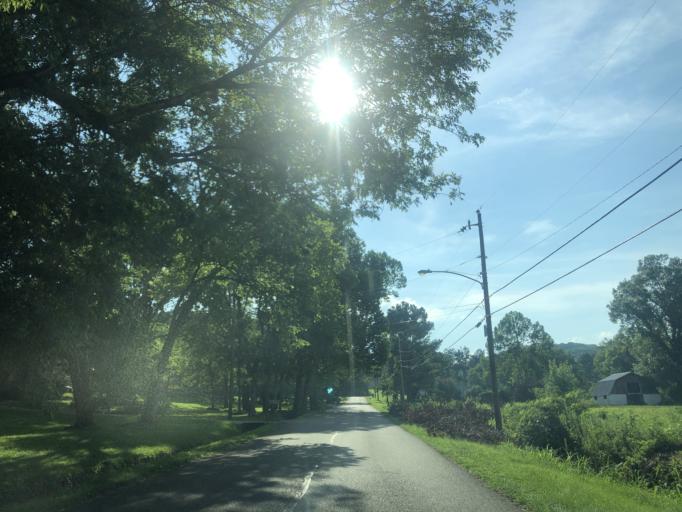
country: US
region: Tennessee
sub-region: Davidson County
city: Nashville
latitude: 36.2382
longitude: -86.8321
